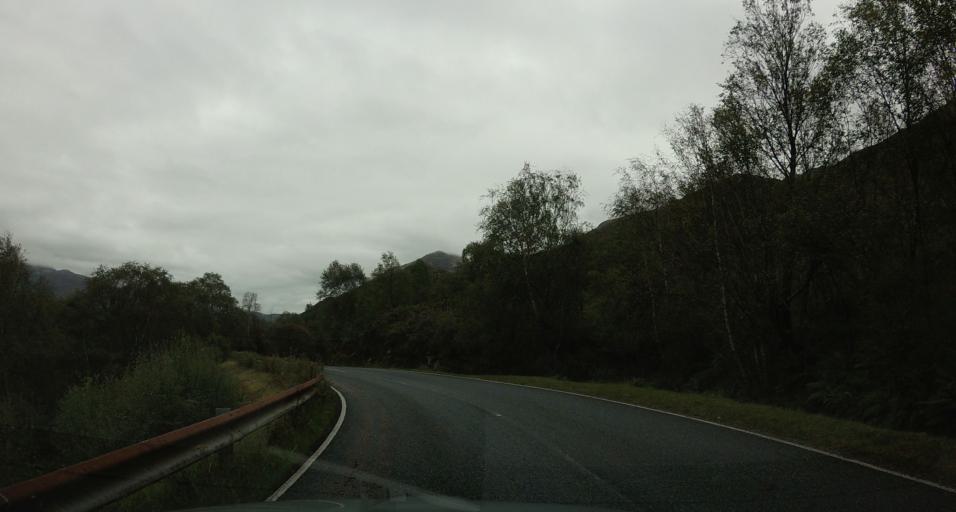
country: GB
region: Scotland
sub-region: Highland
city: Fort William
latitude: 56.6985
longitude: -5.0630
